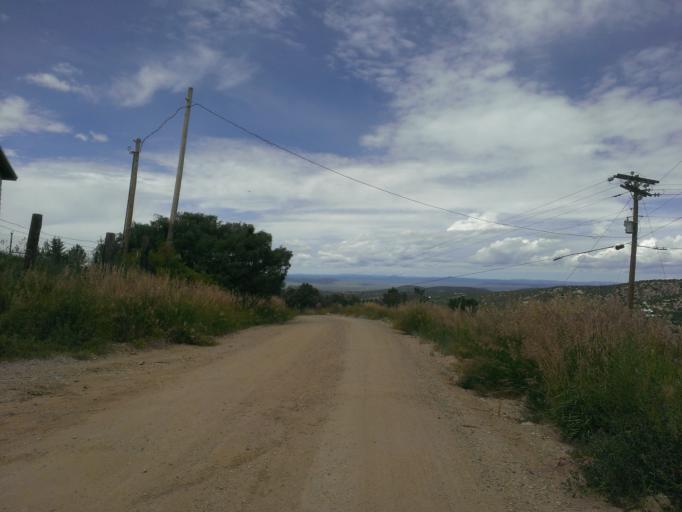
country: US
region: New Mexico
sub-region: Taos County
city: Arroyo Seco
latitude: 36.5347
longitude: -105.5615
